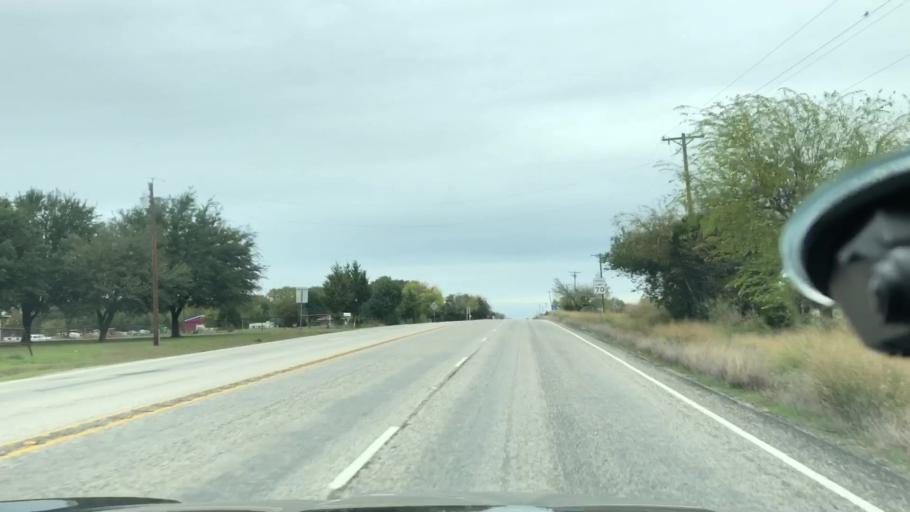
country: US
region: Texas
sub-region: Hunt County
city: Quinlan
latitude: 32.9511
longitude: -96.1077
